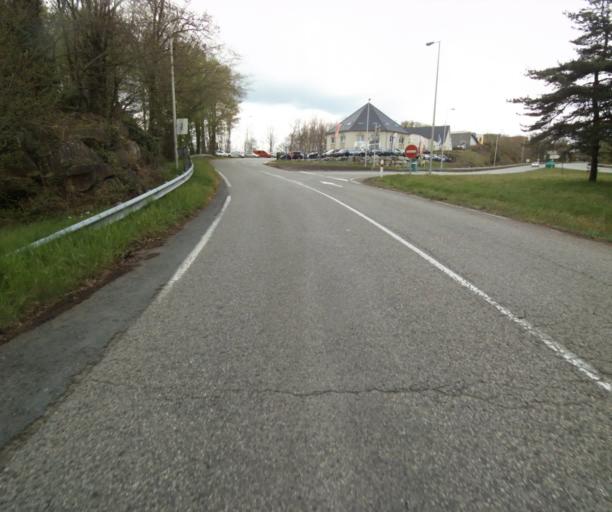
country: FR
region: Limousin
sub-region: Departement de la Correze
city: Tulle
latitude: 45.2781
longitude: 1.7896
